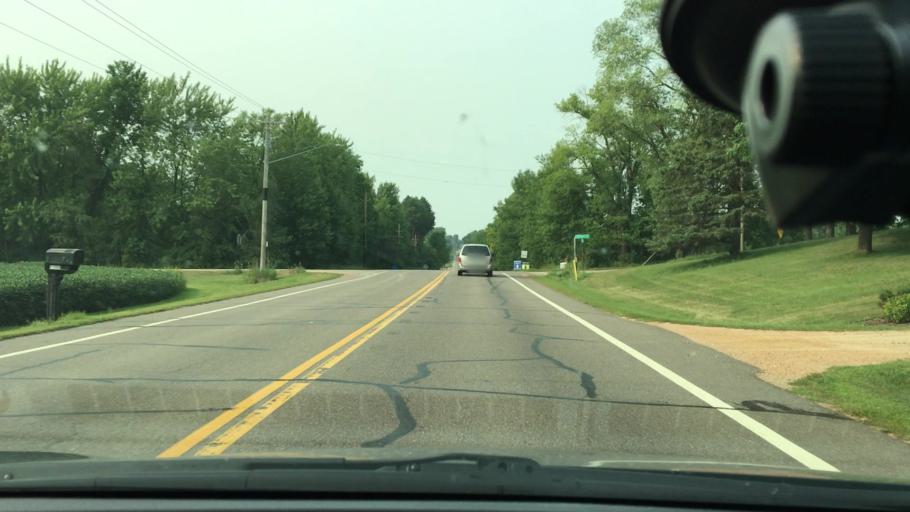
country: US
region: Minnesota
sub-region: Hennepin County
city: Champlin
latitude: 45.1662
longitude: -93.4621
